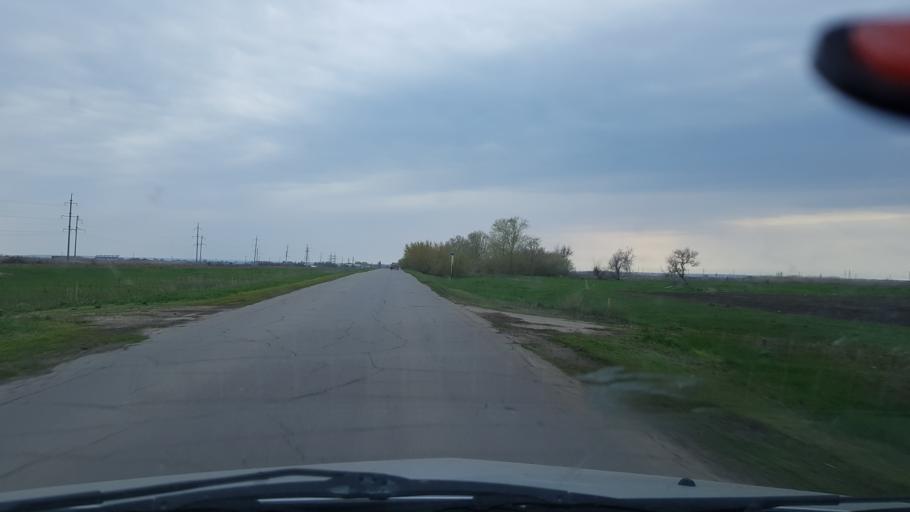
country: RU
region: Samara
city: Khryashchevka
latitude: 53.6707
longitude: 49.1076
